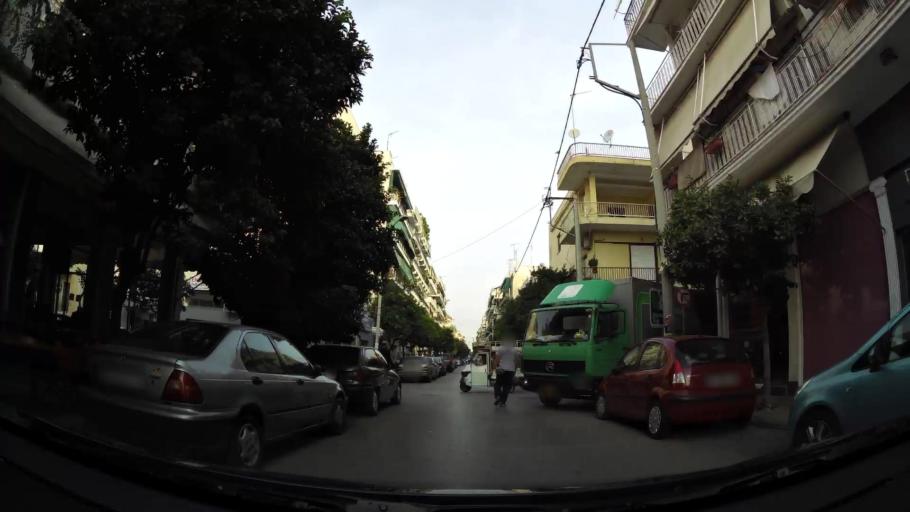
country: GR
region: Attica
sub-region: Nomarchia Athinas
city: Kallithea
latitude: 37.9536
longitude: 23.7028
